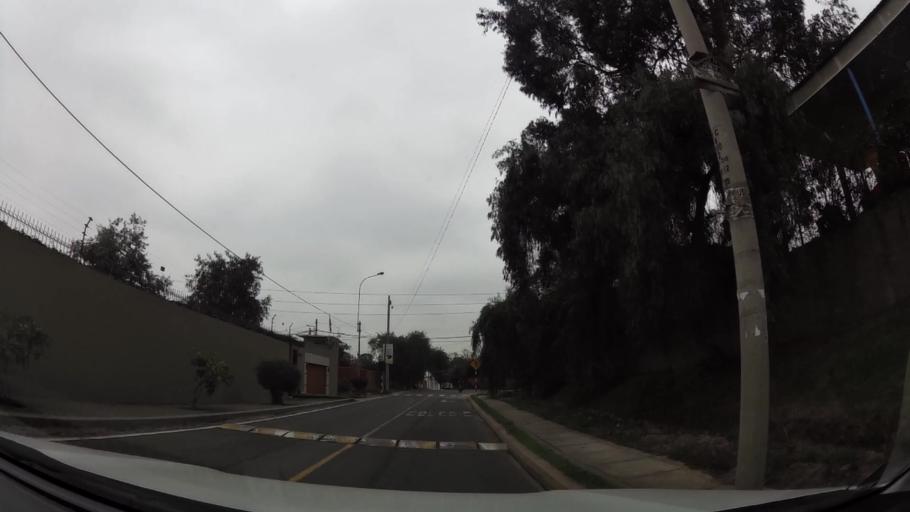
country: PE
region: Lima
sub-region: Lima
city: La Molina
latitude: -12.0798
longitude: -76.9257
